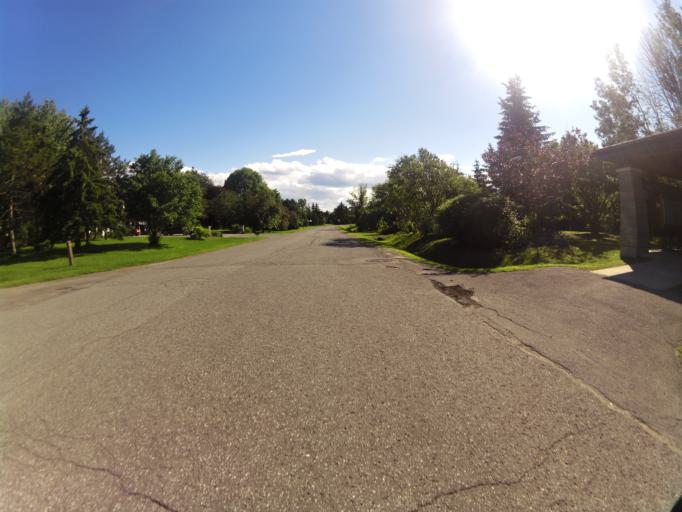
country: CA
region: Ontario
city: Bells Corners
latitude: 45.2794
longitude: -75.7849
